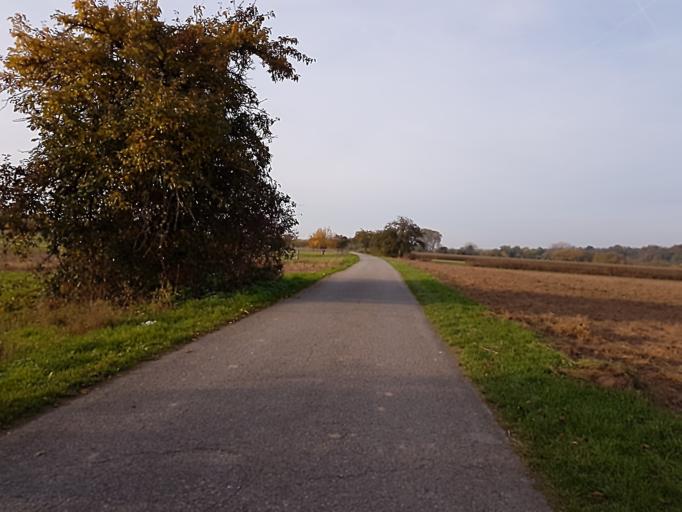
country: DE
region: Bavaria
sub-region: Regierungsbezirk Unterfranken
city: Grosswallstadt
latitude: 49.8878
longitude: 9.1558
